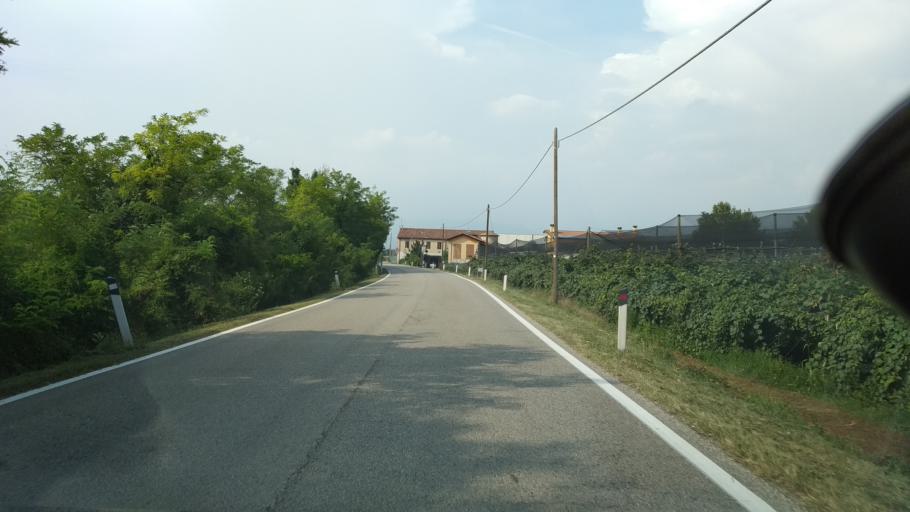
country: IT
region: Veneto
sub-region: Provincia di Vicenza
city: Tezze
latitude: 45.6700
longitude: 11.7111
